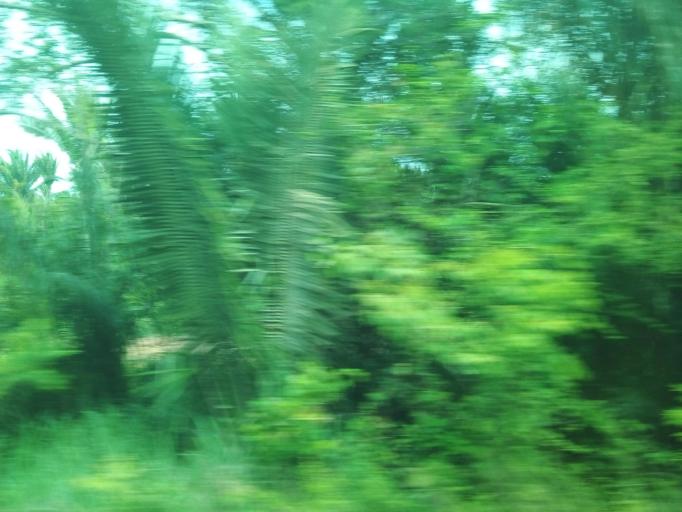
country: BR
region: Maranhao
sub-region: Anajatuba
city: Anajatuba
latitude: -3.4080
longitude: -44.5433
